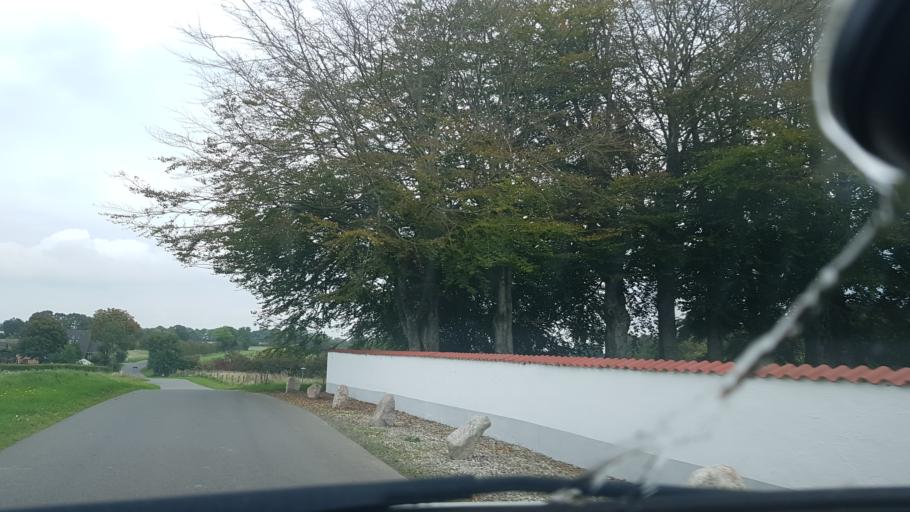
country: DK
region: South Denmark
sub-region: Vejle Kommune
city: Egtved
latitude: 55.5721
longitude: 9.2809
